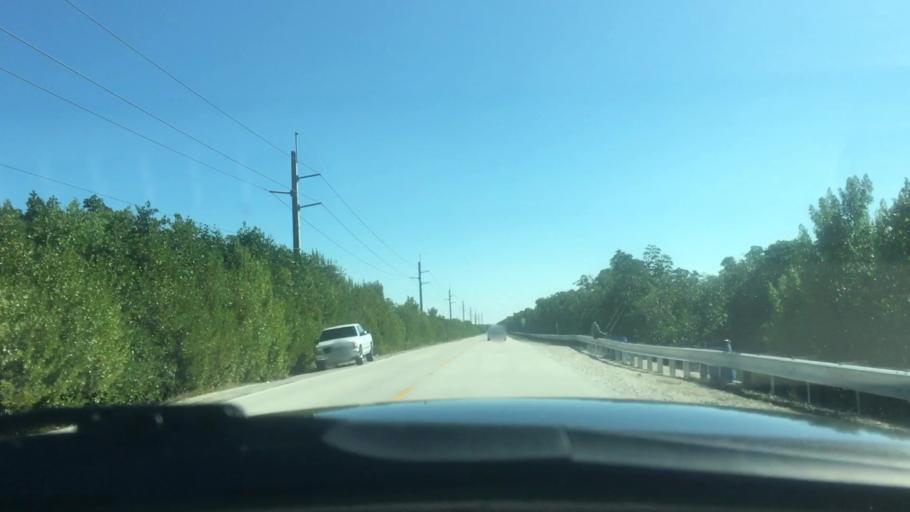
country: US
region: Florida
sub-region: Monroe County
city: North Key Largo
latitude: 25.2815
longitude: -80.3504
